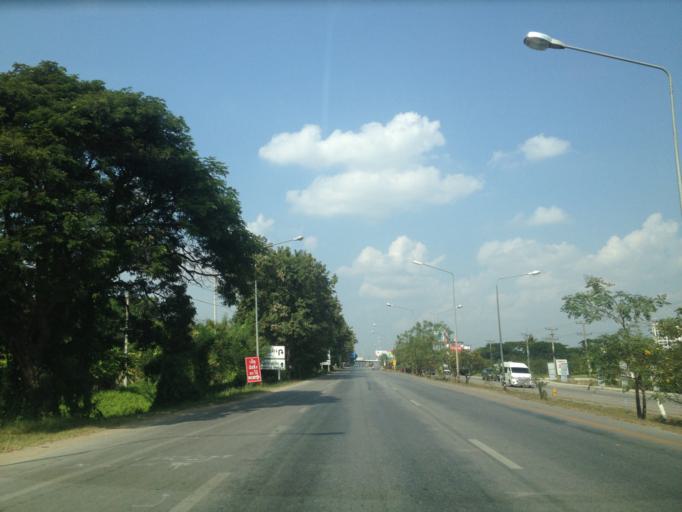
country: TH
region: Chiang Mai
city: Saraphi
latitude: 18.7441
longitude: 99.0347
